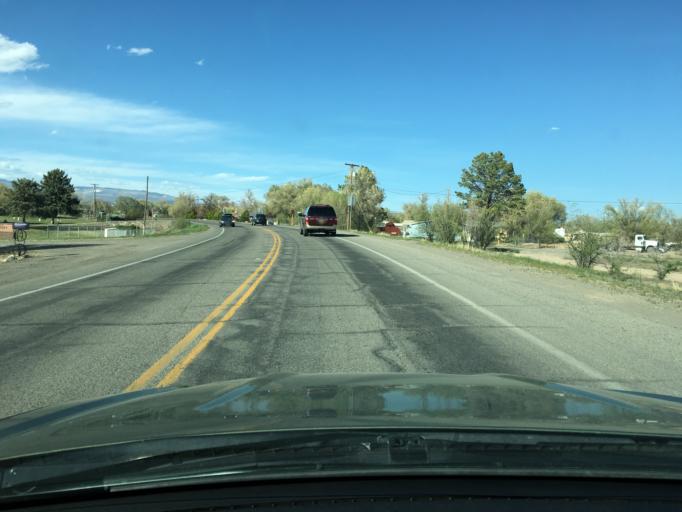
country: US
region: Colorado
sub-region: Delta County
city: Orchard City
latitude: 38.7894
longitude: -107.9891
